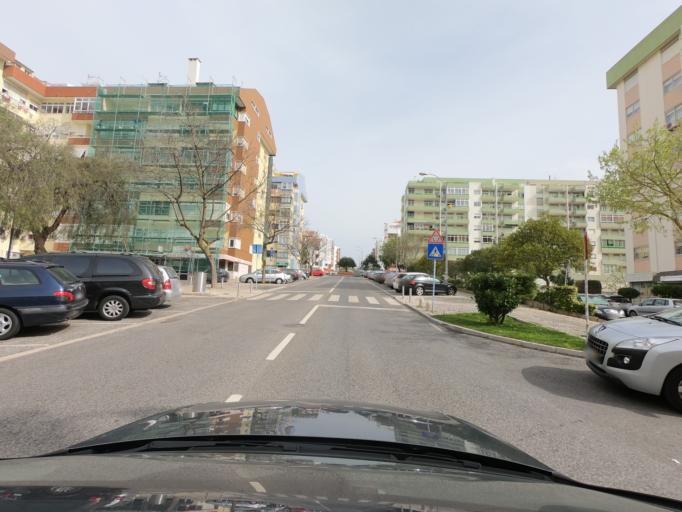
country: PT
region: Lisbon
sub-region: Oeiras
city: Oeiras
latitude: 38.6968
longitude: -9.3026
